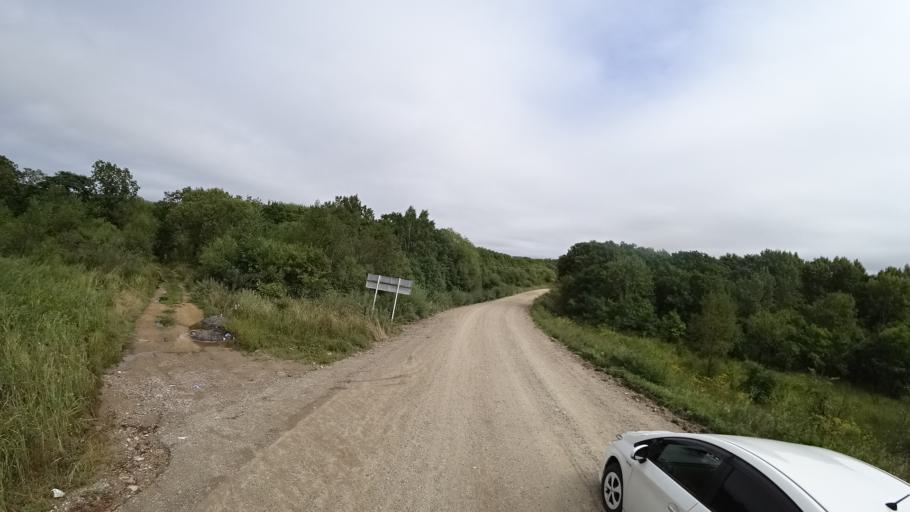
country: RU
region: Primorskiy
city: Lyalichi
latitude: 44.0996
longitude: 132.4251
